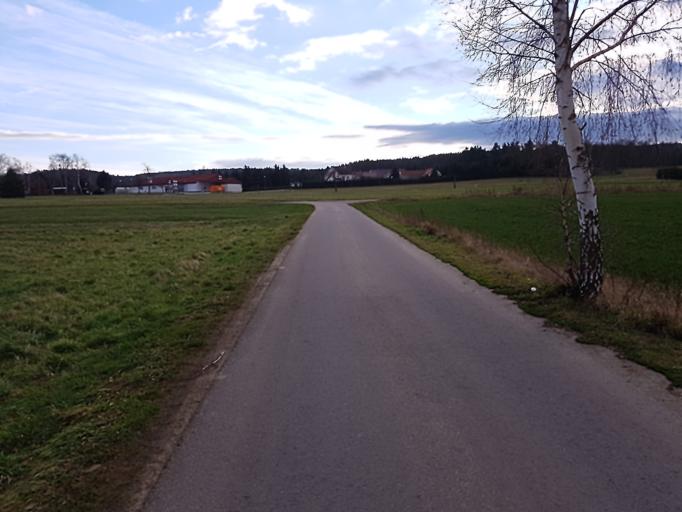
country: DE
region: Brandenburg
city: Groden
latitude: 51.4066
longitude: 13.5614
